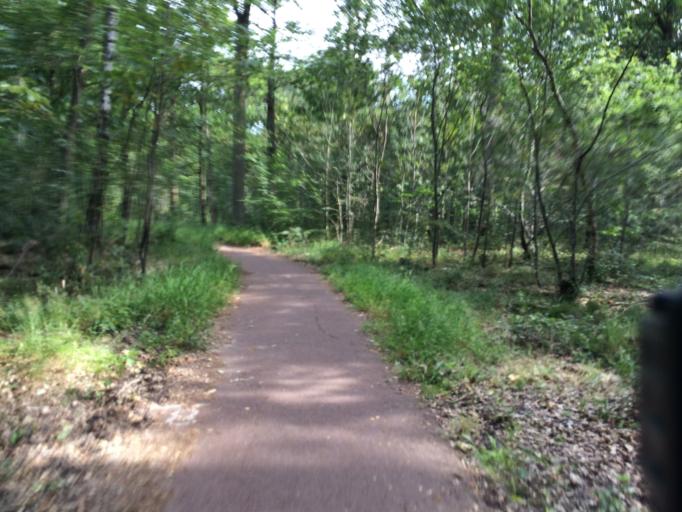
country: FR
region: Ile-de-France
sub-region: Departement de l'Essonne
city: Brunoy
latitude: 48.6657
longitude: 2.4901
